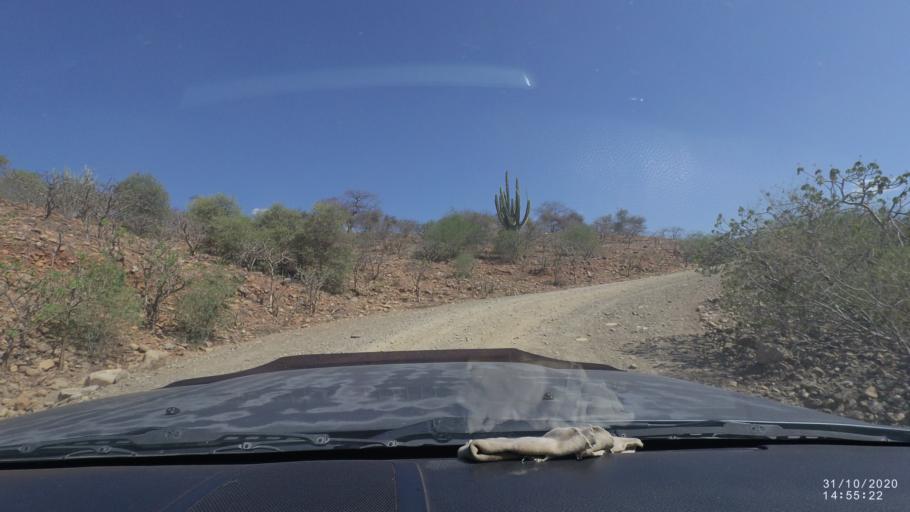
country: BO
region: Cochabamba
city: Aiquile
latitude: -18.2322
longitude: -64.8567
